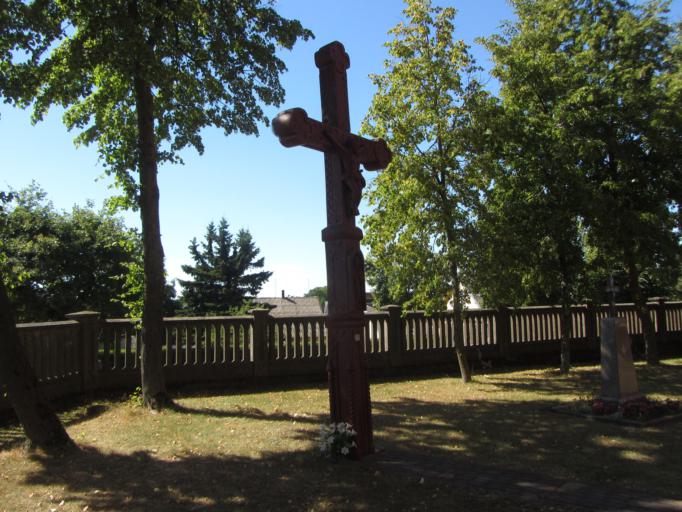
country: LT
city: Kupiskis
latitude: 55.8415
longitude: 24.9759
